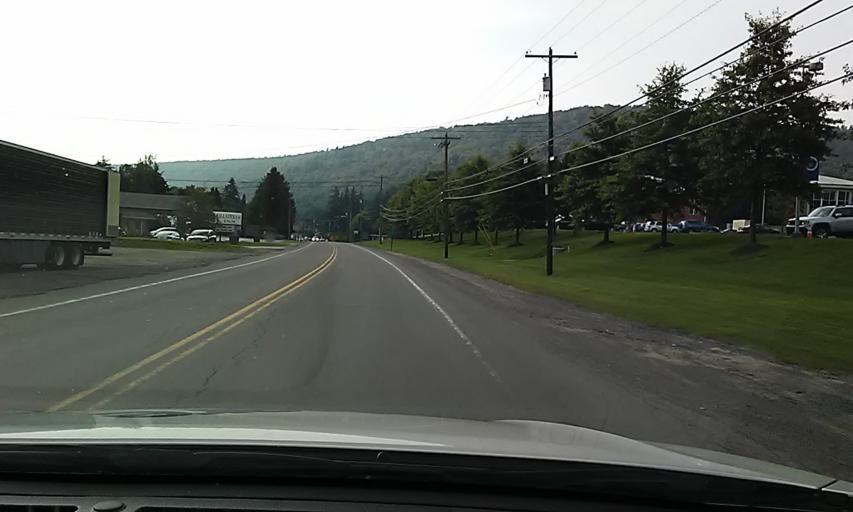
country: US
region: Pennsylvania
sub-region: Potter County
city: Coudersport
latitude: 41.7703
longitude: -77.9791
